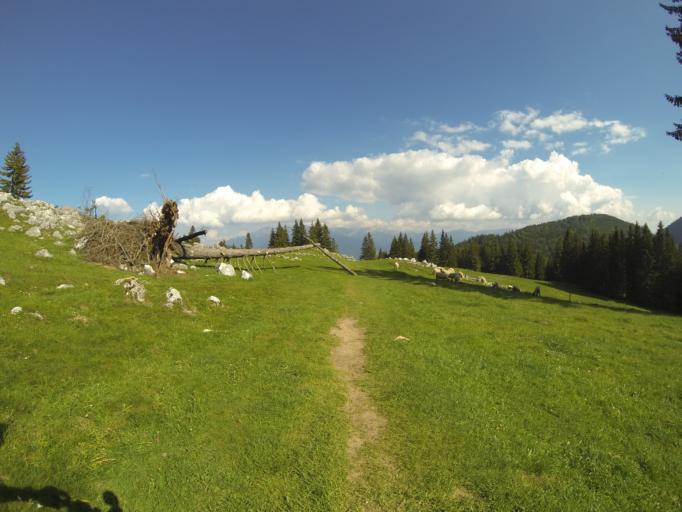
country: RO
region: Brasov
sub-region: Comuna Zarnesti
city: Zarnesti
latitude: 45.5408
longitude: 25.2741
